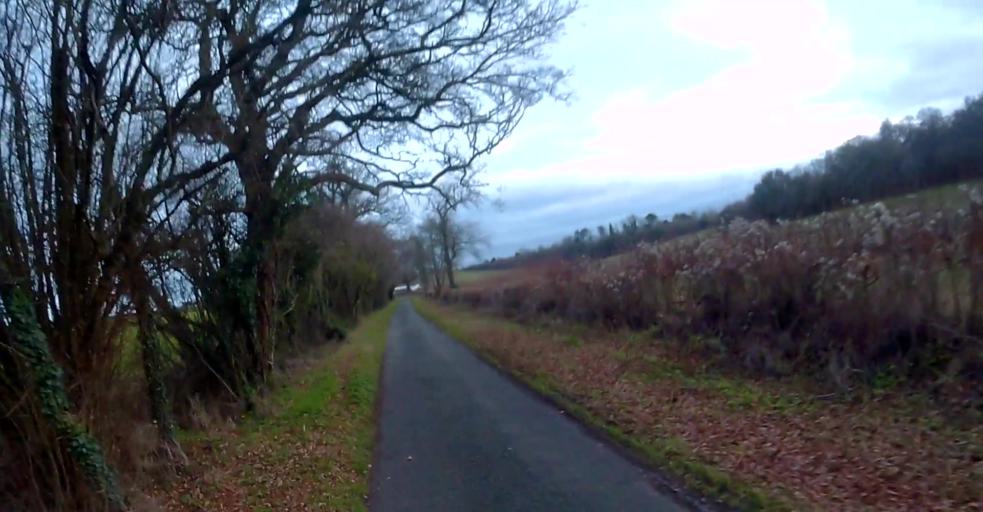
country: GB
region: England
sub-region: Hampshire
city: Overton
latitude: 51.2593
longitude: -1.2354
